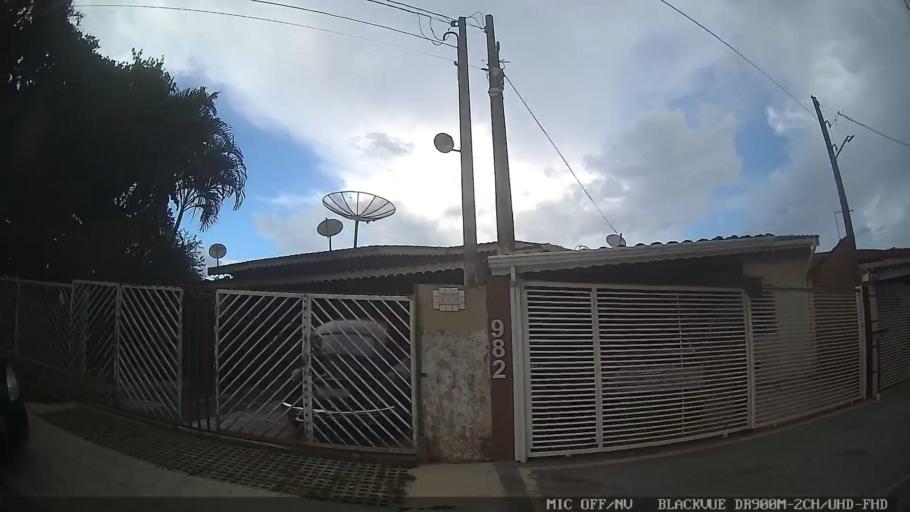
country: BR
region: Sao Paulo
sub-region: Atibaia
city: Atibaia
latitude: -23.1091
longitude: -46.5146
